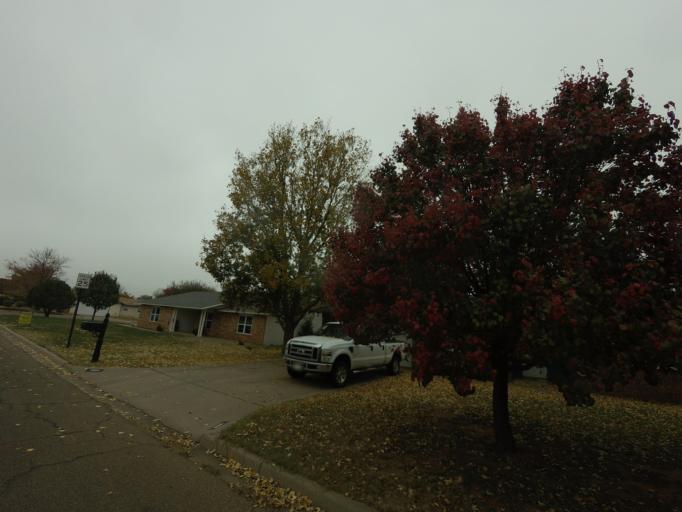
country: US
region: New Mexico
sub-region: Curry County
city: Clovis
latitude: 34.4262
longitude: -103.1825
